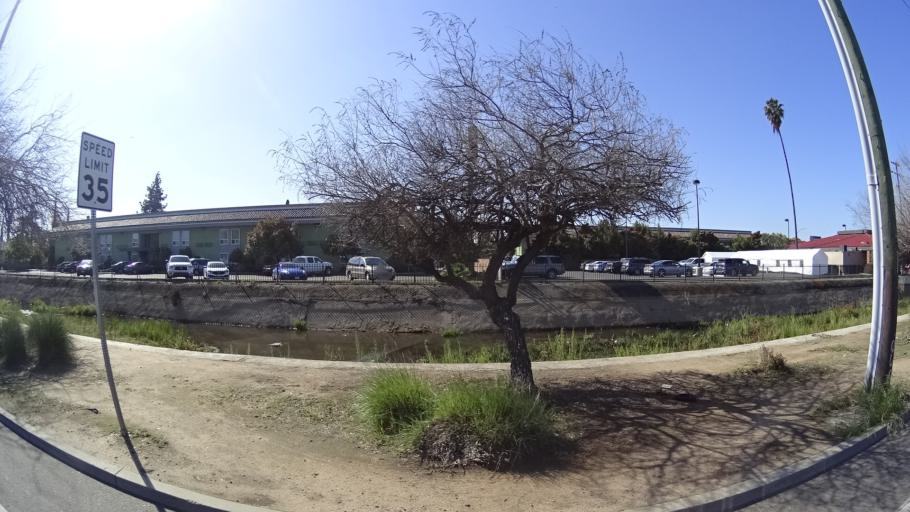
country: US
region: California
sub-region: Fresno County
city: Fresno
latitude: 36.7796
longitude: -119.7896
